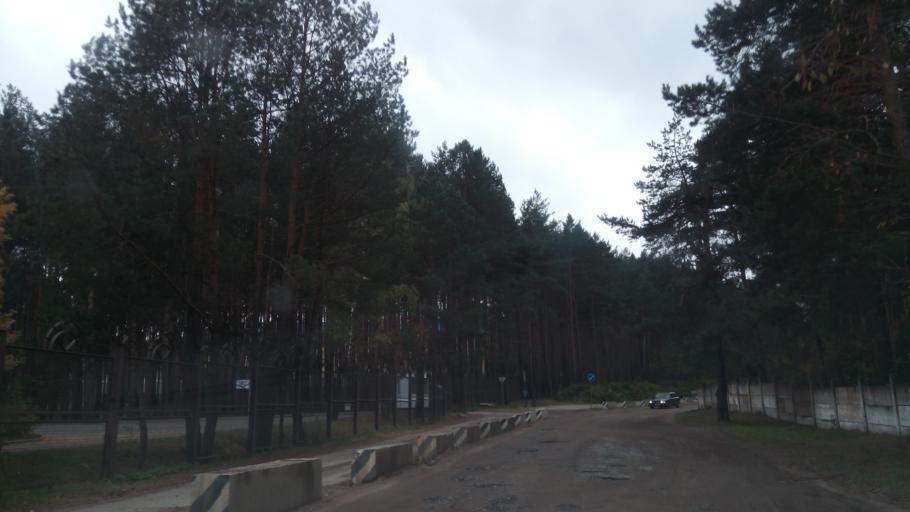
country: BY
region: Minsk
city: Zhdanovichy
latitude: 53.9567
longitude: 27.4412
